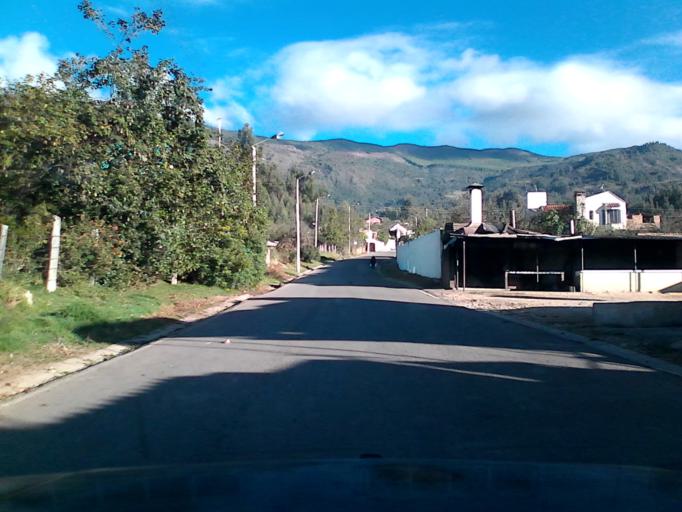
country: CO
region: Boyaca
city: Duitama
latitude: 5.8629
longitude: -73.0311
